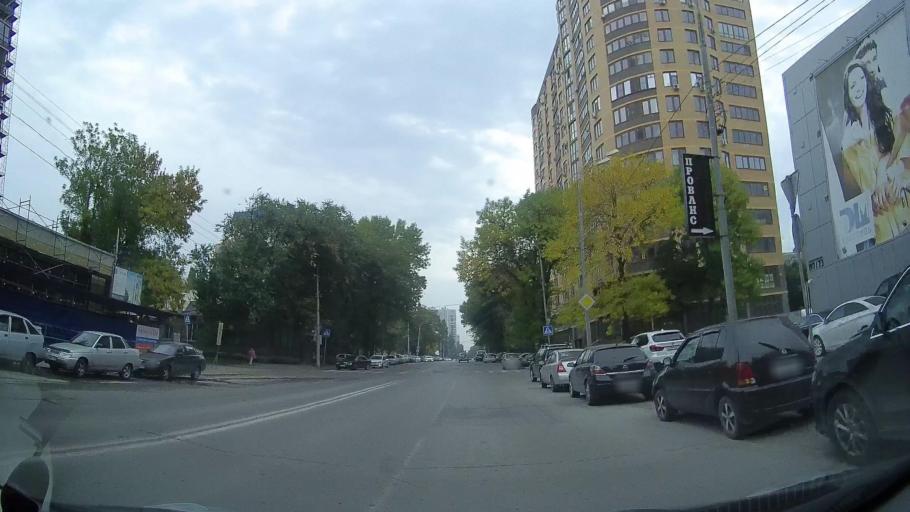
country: RU
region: Rostov
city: Rostov-na-Donu
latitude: 47.2340
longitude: 39.7265
